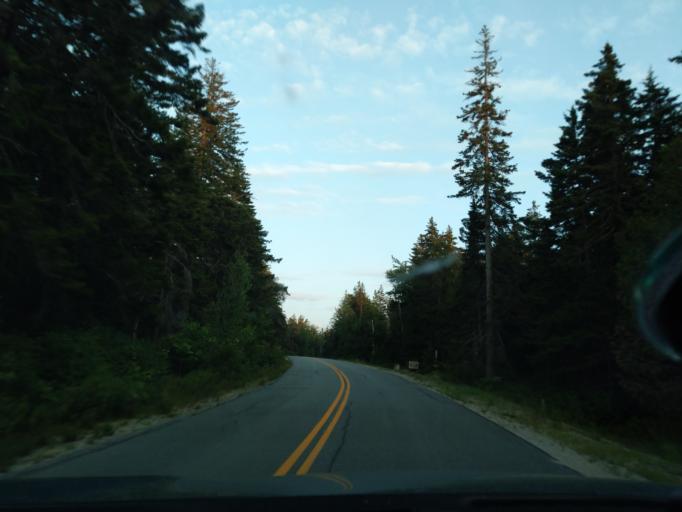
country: US
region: Maine
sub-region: Hancock County
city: Gouldsboro
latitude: 44.3897
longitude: -68.0723
